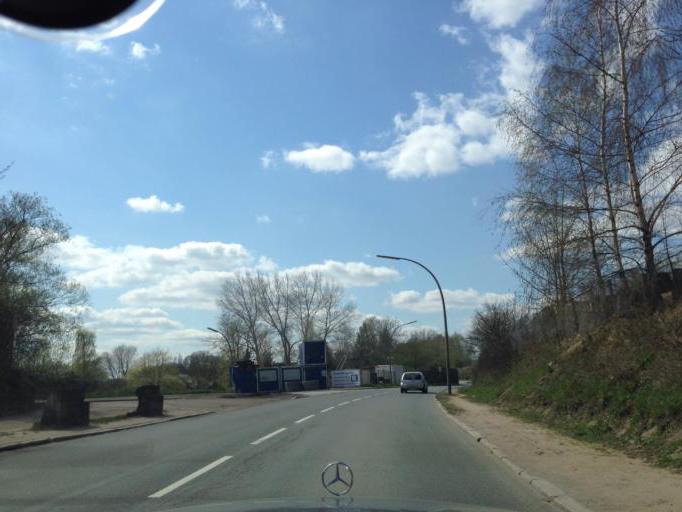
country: DE
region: Hamburg
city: Wandsbek
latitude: 53.5194
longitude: 10.1005
